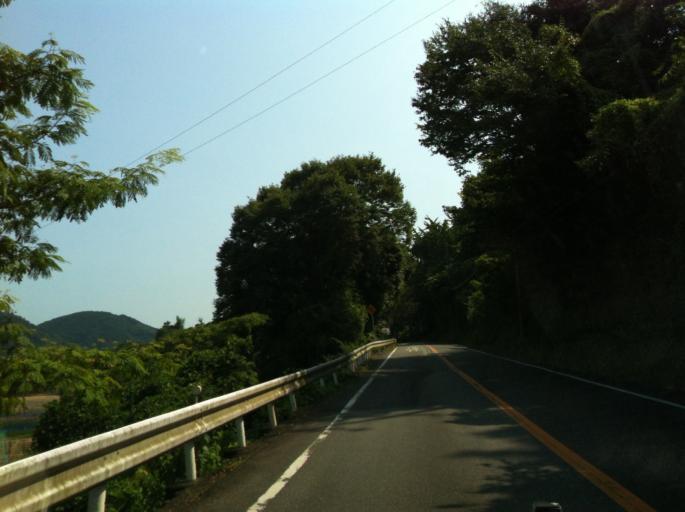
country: JP
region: Shizuoka
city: Shizuoka-shi
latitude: 35.0839
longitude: 138.3693
